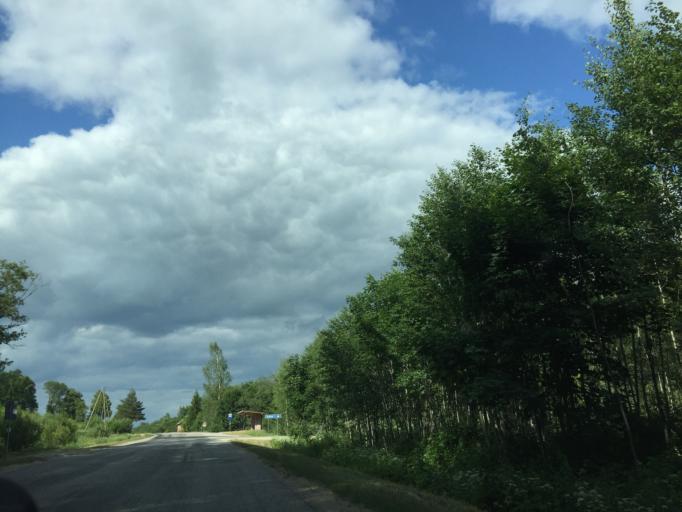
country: LV
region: Skriveri
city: Skriveri
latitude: 56.8090
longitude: 25.1124
